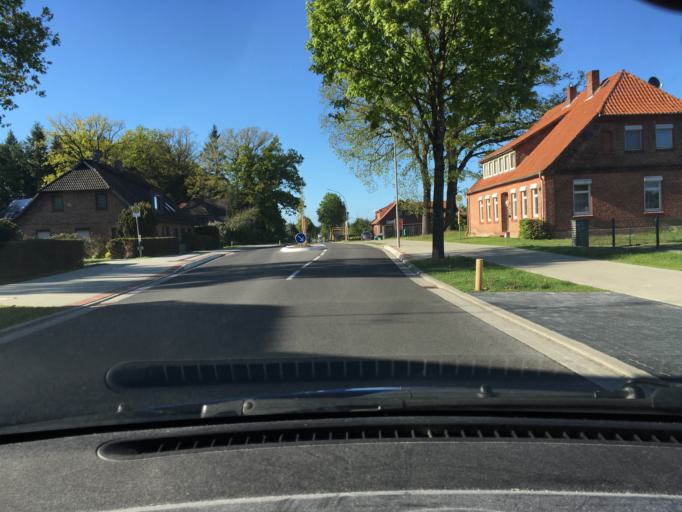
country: DE
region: Lower Saxony
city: Schneverdingen
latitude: 53.0744
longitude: 9.8634
